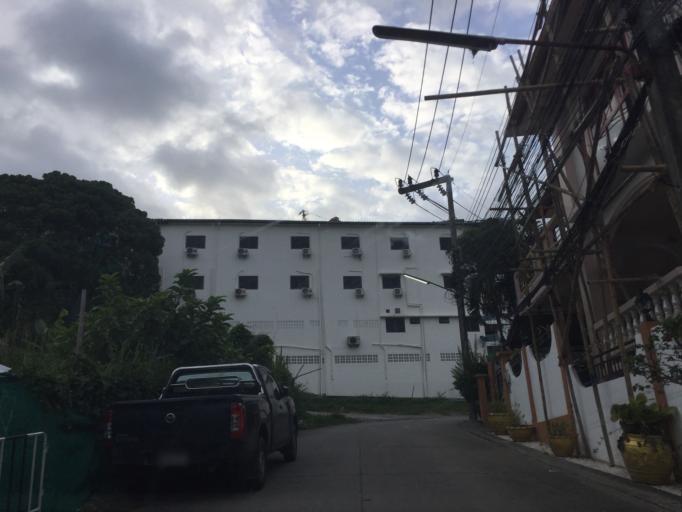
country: TH
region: Phuket
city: Patong
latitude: 7.8928
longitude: 98.3040
